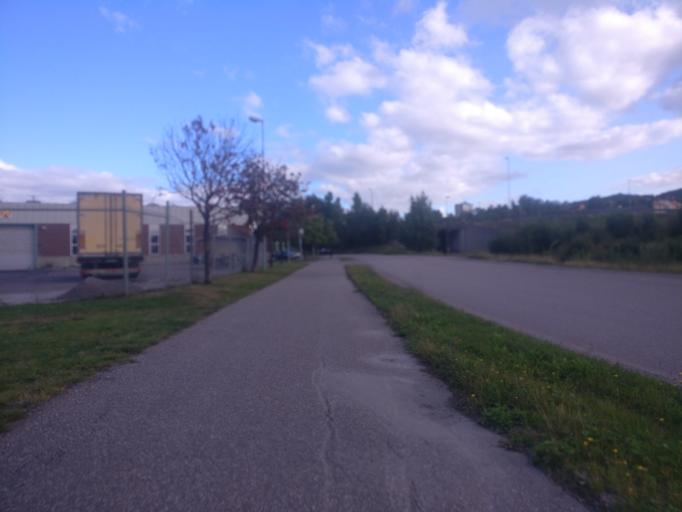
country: SE
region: Vaesternorrland
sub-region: Sundsvalls Kommun
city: Sundsvall
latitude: 62.3862
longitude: 17.3284
